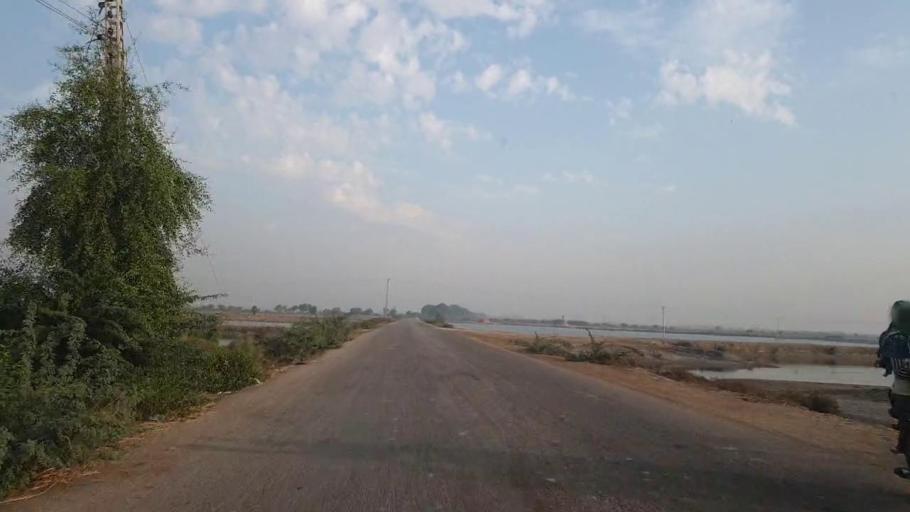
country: PK
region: Sindh
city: Tando Bago
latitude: 24.7213
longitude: 68.9421
